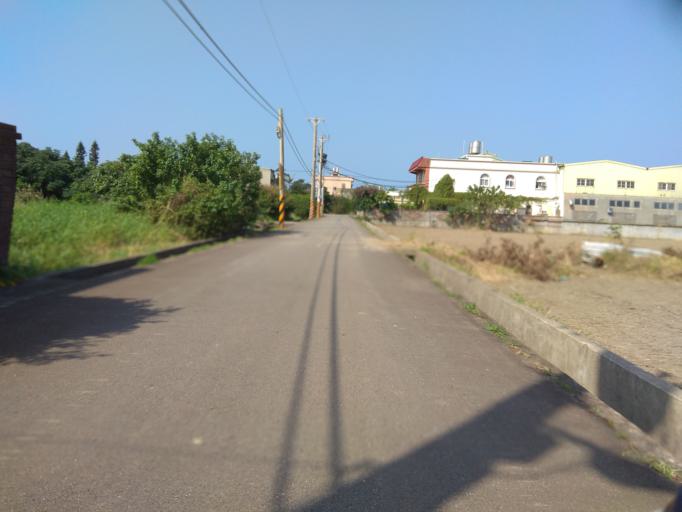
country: TW
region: Taiwan
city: Taoyuan City
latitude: 25.0495
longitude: 121.2155
